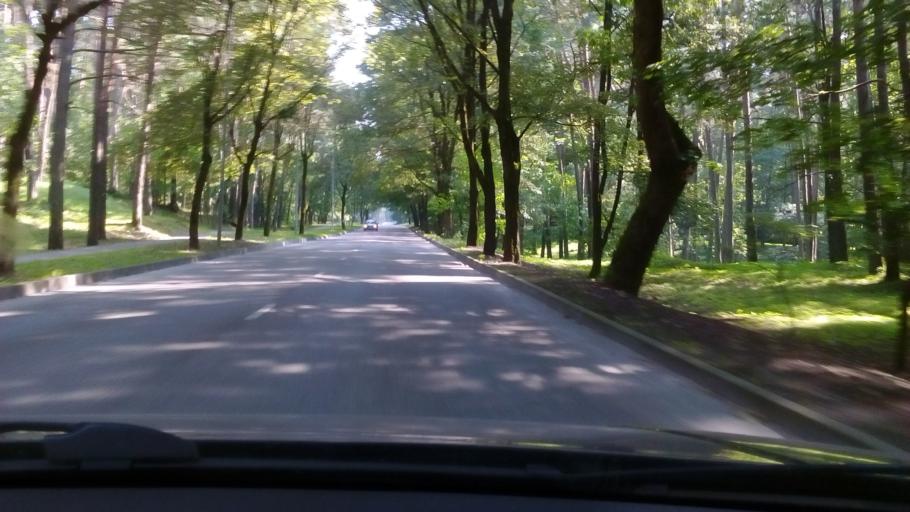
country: LT
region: Alytaus apskritis
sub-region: Alytus
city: Alytus
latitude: 54.3957
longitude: 24.0543
